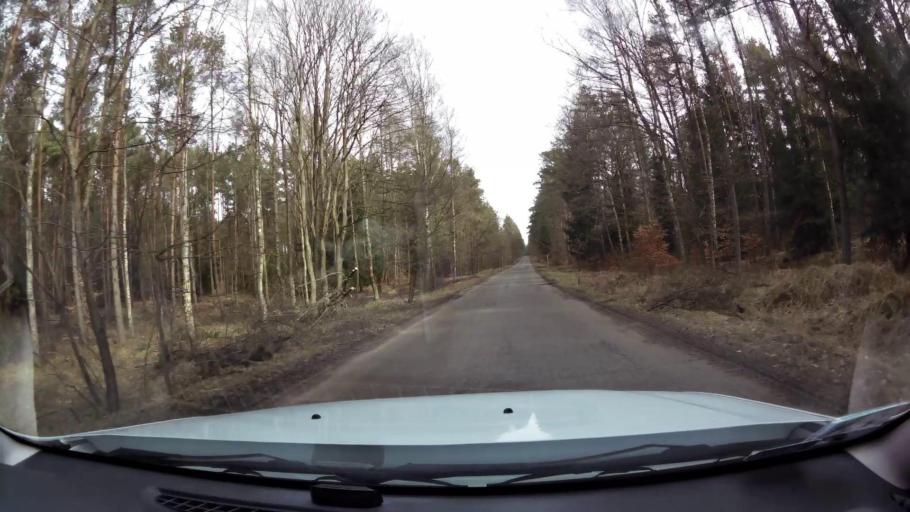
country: PL
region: West Pomeranian Voivodeship
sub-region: Powiat stargardzki
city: Insko
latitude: 53.4617
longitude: 15.6669
